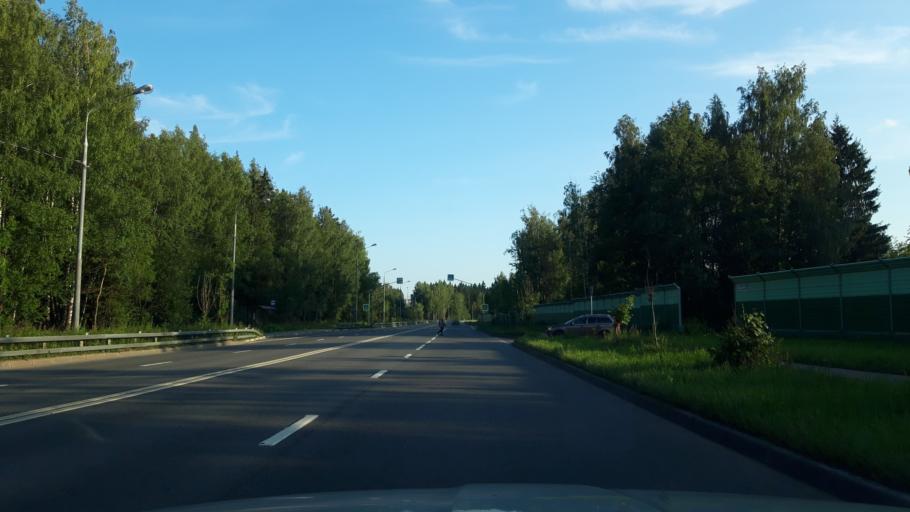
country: RU
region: Moskovskaya
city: Alabushevo
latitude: 56.0023
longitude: 37.1634
